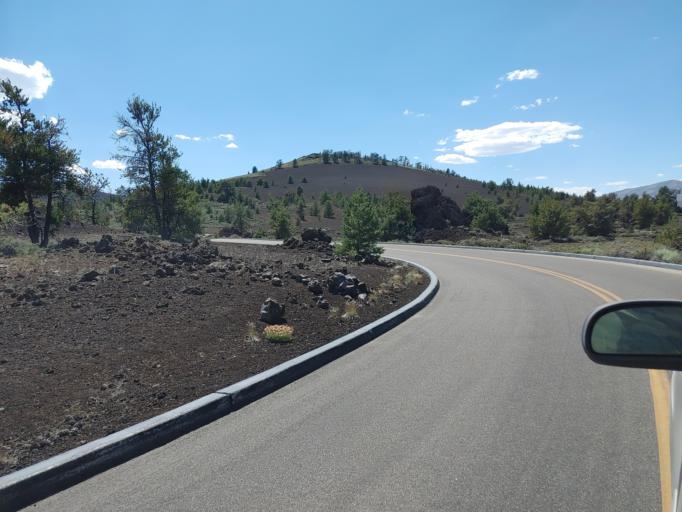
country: US
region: Idaho
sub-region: Butte County
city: Arco
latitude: 43.4528
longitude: -113.5409
